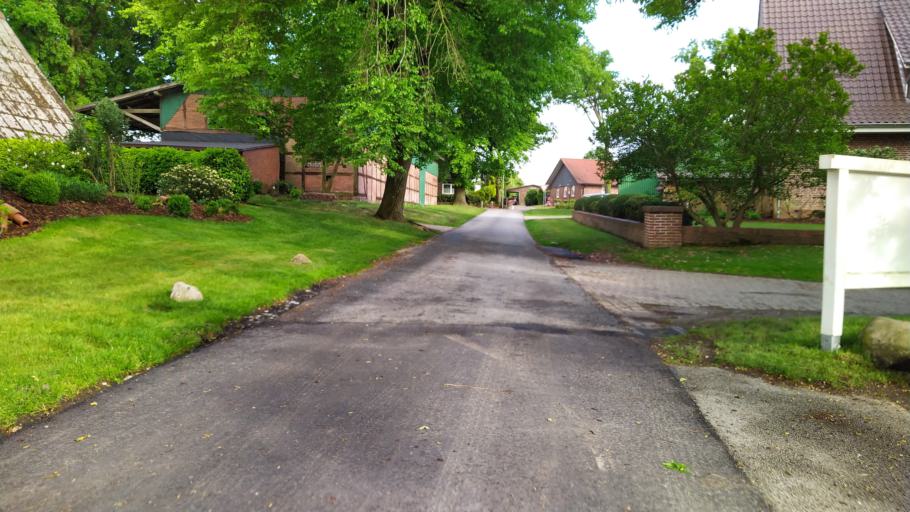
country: DE
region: Lower Saxony
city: Farven
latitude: 53.4355
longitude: 9.3219
